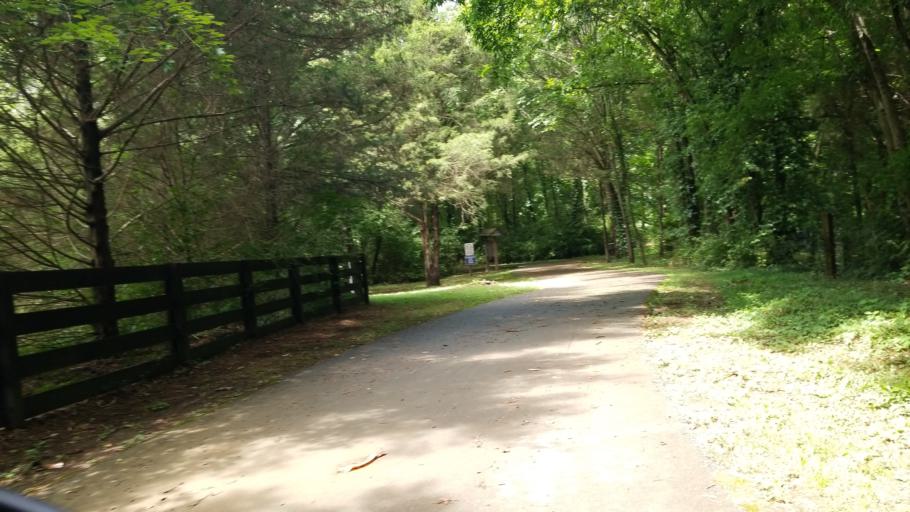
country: US
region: Tennessee
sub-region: Davidson County
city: Forest Hills
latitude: 36.0337
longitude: -86.8359
